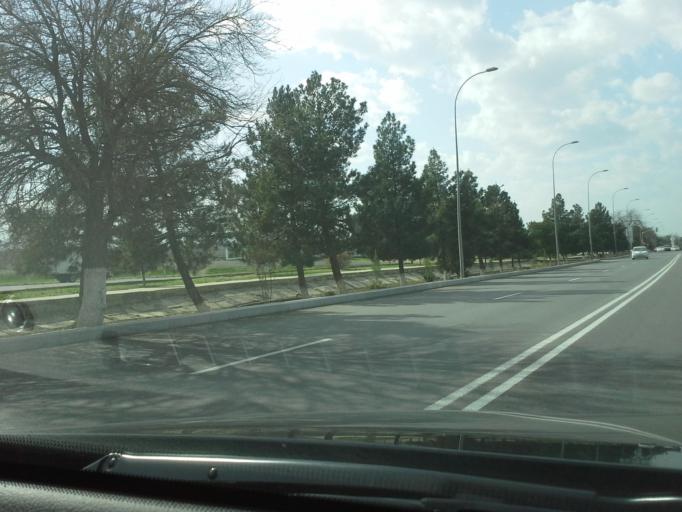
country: TM
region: Ahal
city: Ashgabat
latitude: 37.9571
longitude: 58.3247
